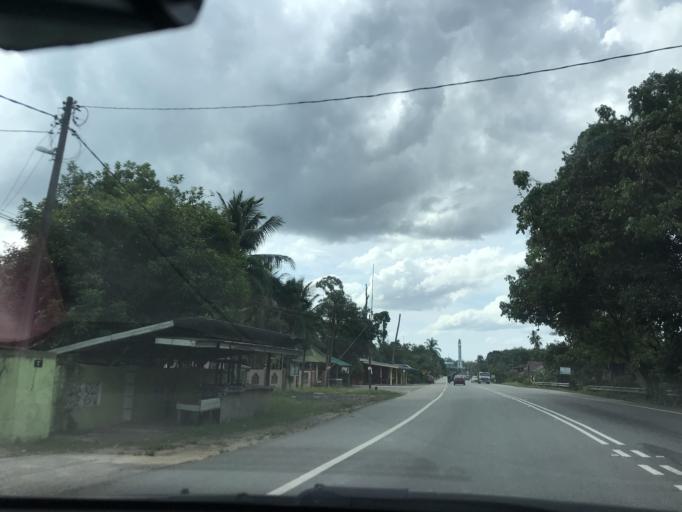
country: MY
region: Kelantan
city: Kampong Pangkal Kalong
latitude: 5.9388
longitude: 102.1919
